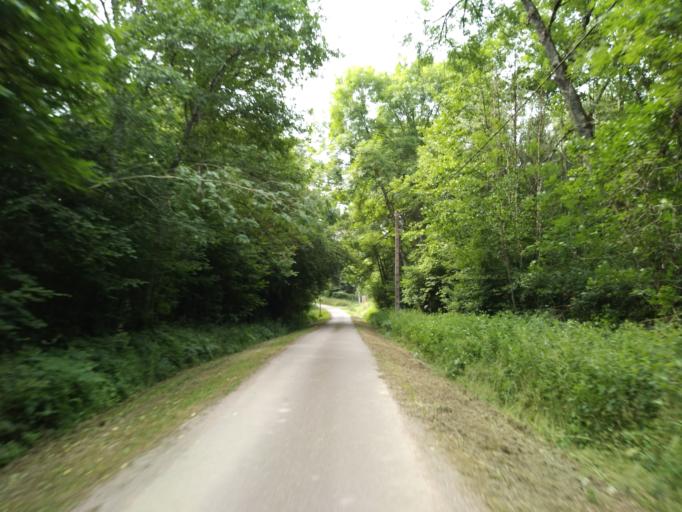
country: FR
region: Bourgogne
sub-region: Departement de la Cote-d'Or
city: Saulieu
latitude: 47.2814
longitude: 4.1218
